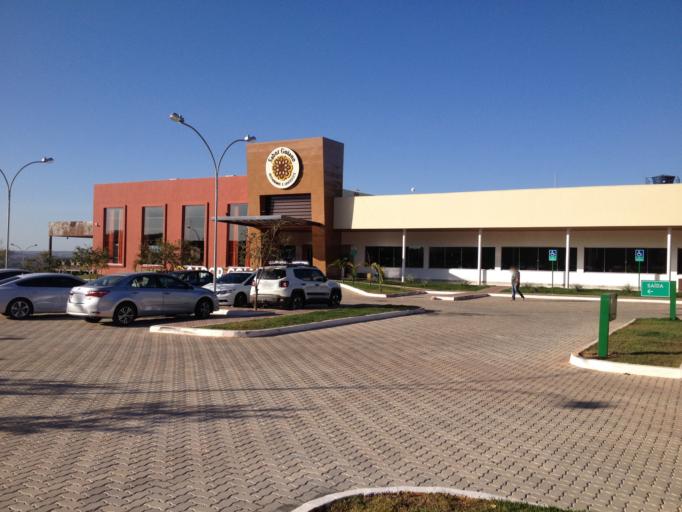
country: BR
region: Goias
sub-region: Abadiania
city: Abadiania
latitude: -16.1913
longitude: -48.6716
